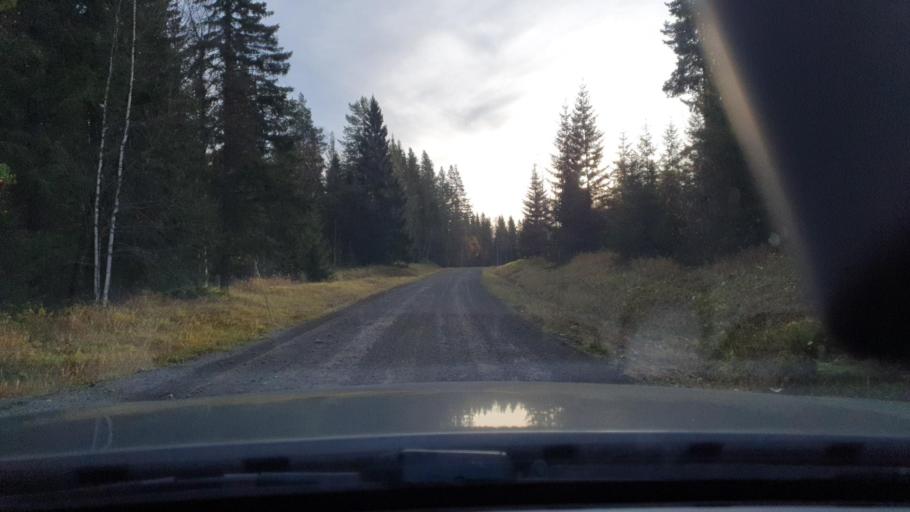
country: SE
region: Jaemtland
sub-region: Stroemsunds Kommun
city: Stroemsund
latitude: 63.5308
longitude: 15.6190
